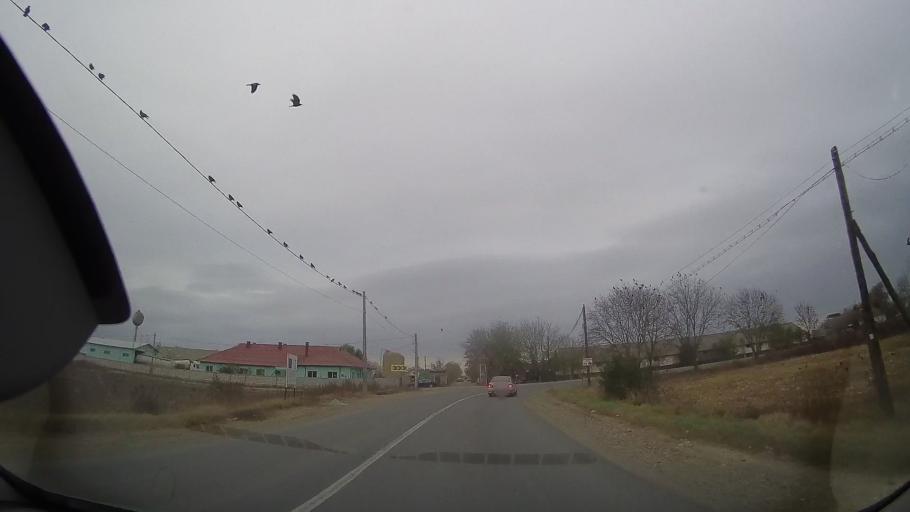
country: RO
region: Ialomita
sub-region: Oras Amara
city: Amara
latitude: 44.6211
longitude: 27.3026
